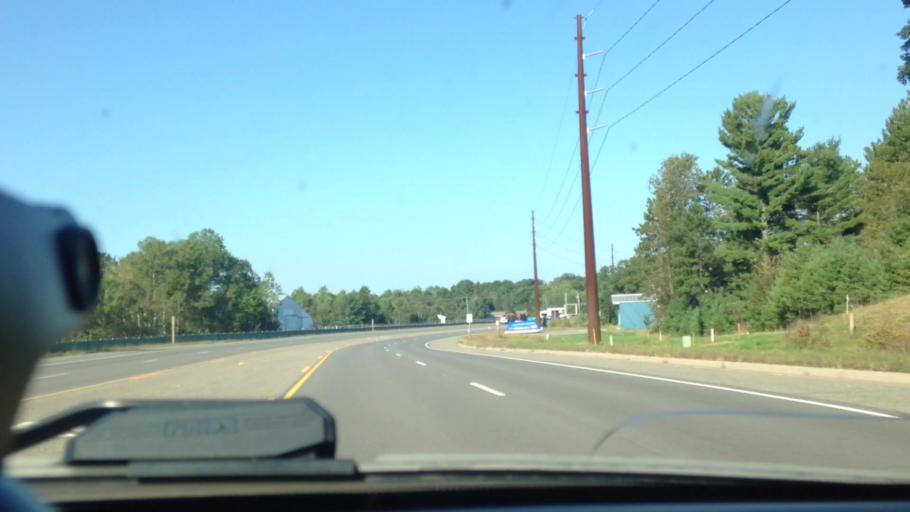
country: US
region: Michigan
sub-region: Dickinson County
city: Iron Mountain
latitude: 45.8820
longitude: -88.1375
